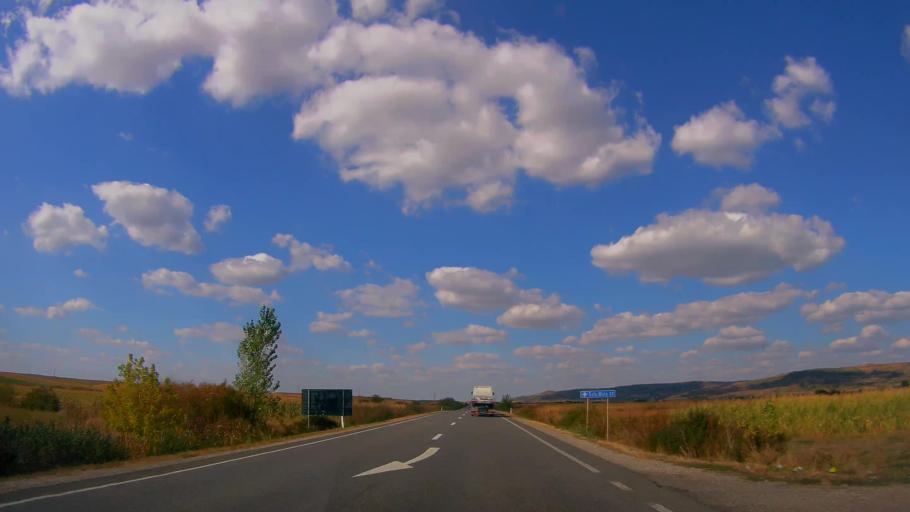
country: RO
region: Salaj
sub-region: Comuna Sarmasag
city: Sarmasag
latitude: 47.3521
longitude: 22.8000
